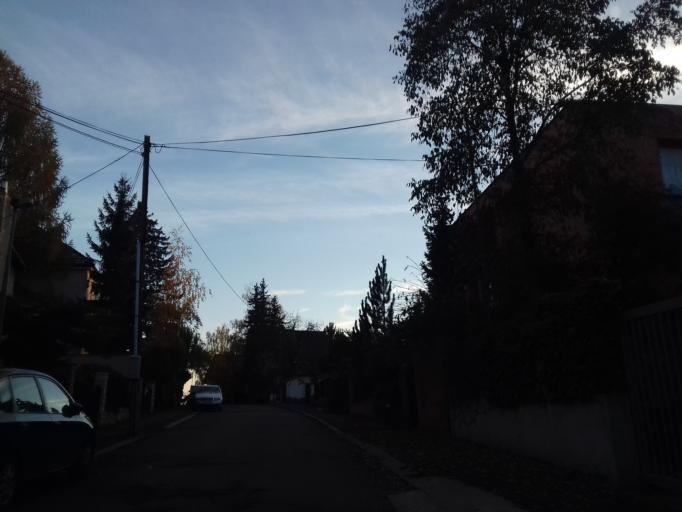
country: CZ
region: Praha
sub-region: Praha 4
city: Hodkovicky
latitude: 50.0264
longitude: 14.4096
